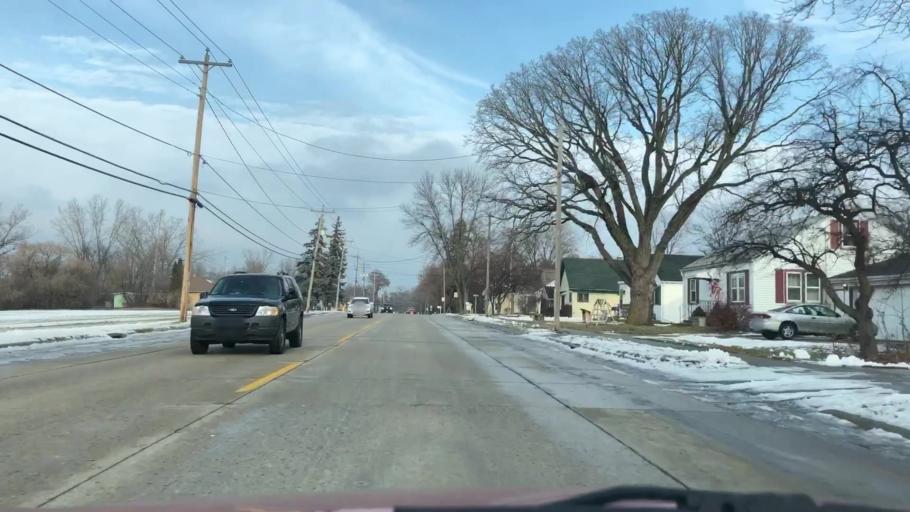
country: US
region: Wisconsin
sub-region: Brown County
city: De Pere
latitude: 44.4341
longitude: -88.0748
